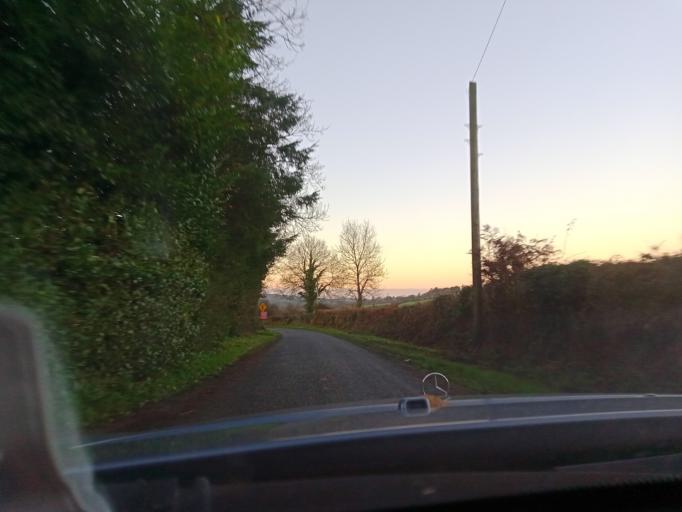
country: IE
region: Leinster
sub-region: Kilkenny
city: Thomastown
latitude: 52.4309
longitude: -7.1014
